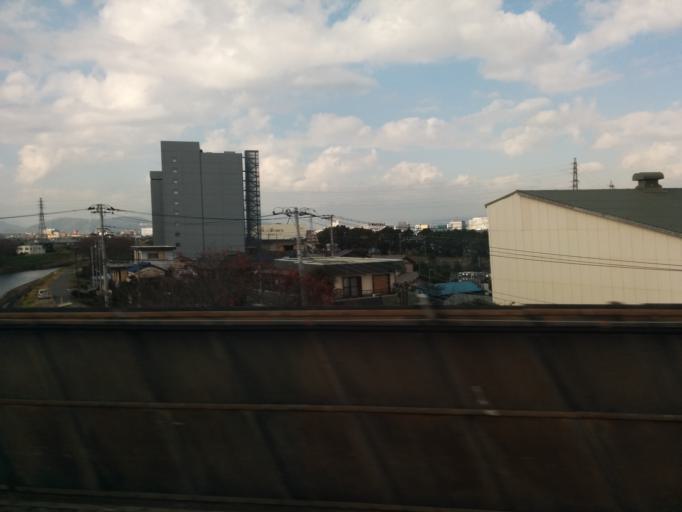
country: JP
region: Shizuoka
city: Fuji
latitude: 35.1460
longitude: 138.6828
